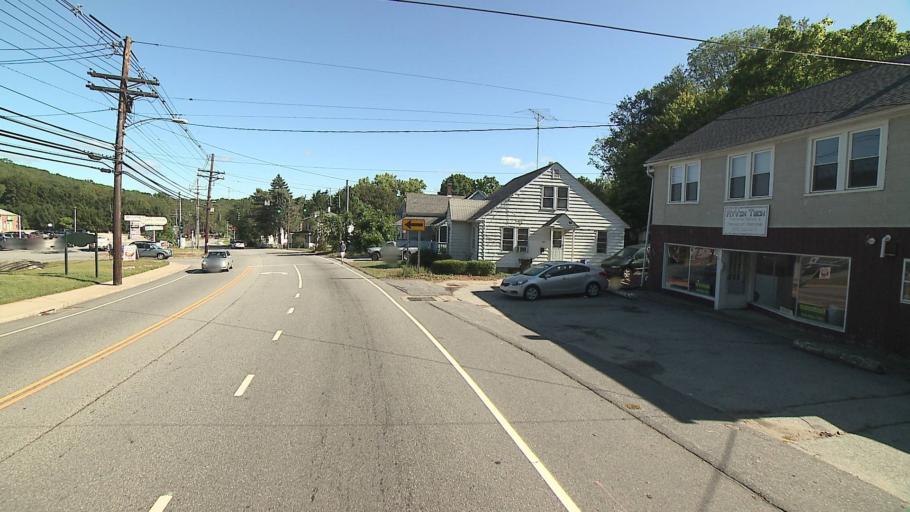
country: US
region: Connecticut
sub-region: New London County
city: Norwich
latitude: 41.5508
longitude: -72.0521
